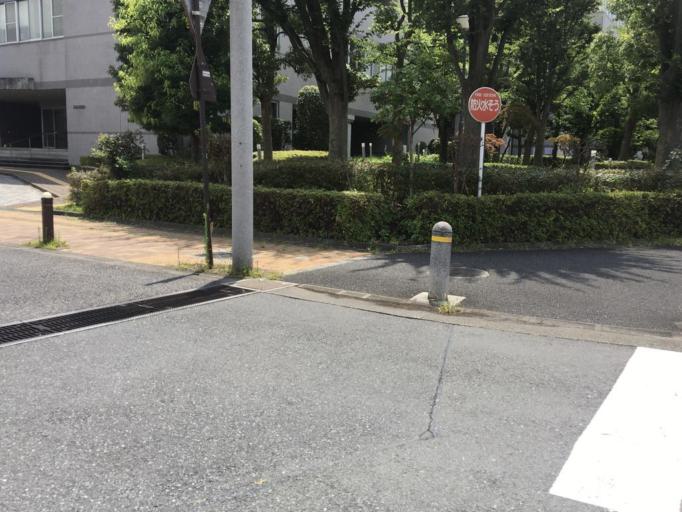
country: JP
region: Saitama
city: Wako
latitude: 35.7821
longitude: 139.6056
